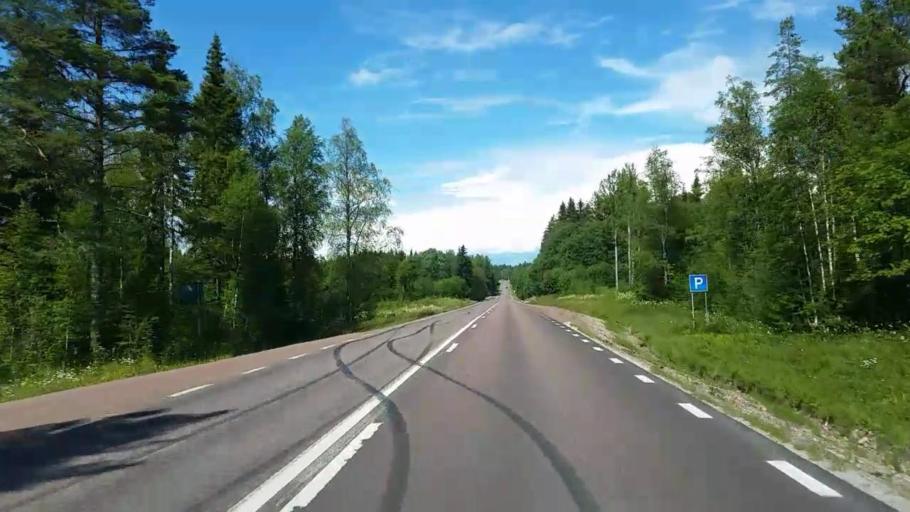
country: SE
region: Dalarna
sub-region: Rattviks Kommun
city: Raettvik
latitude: 61.0274
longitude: 15.2085
